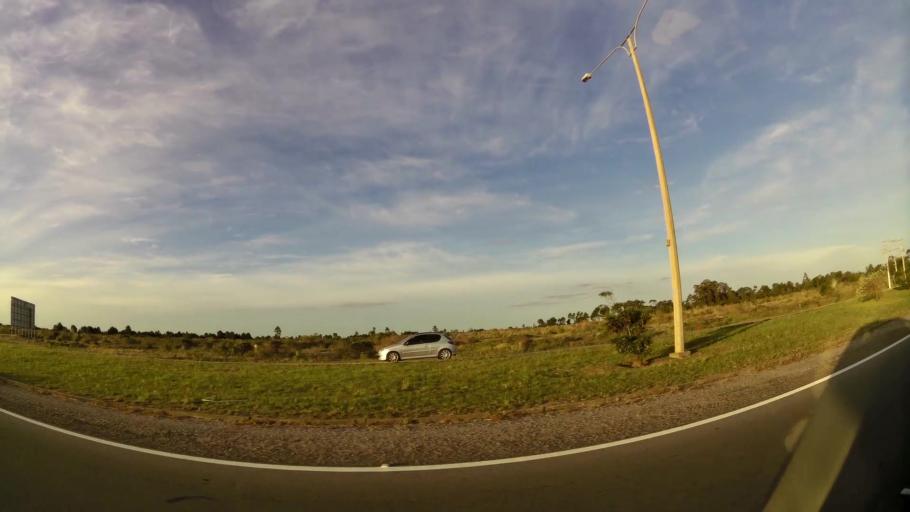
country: UY
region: Canelones
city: Atlantida
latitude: -34.7665
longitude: -55.7851
